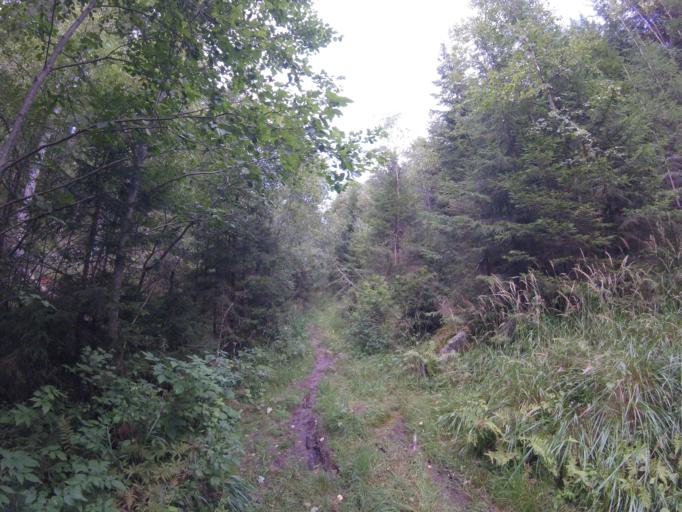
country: NO
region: Akershus
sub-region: Raelingen
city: Fjerdingby
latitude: 59.9177
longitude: 11.0326
